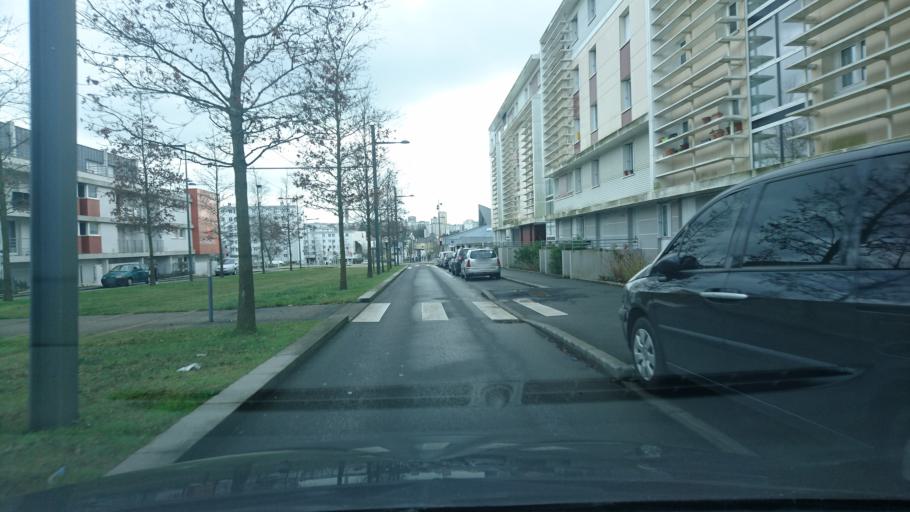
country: FR
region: Brittany
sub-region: Departement du Finistere
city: Brest
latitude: 48.4131
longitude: -4.4715
